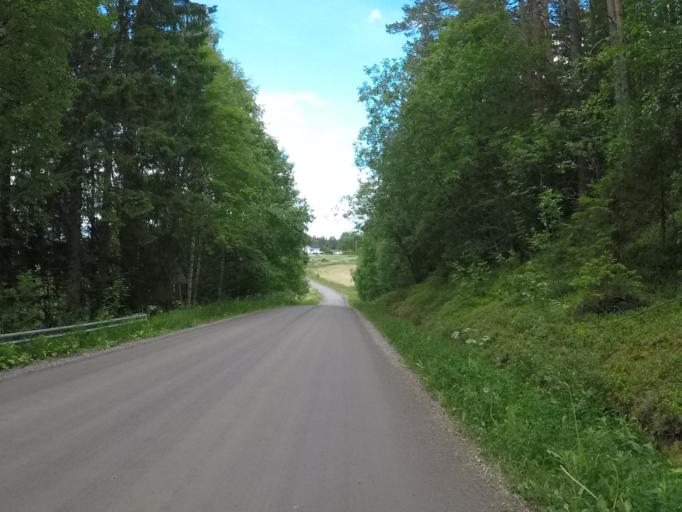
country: SE
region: Vaesterbotten
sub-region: Robertsfors Kommun
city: Robertsfors
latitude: 64.1538
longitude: 20.9153
